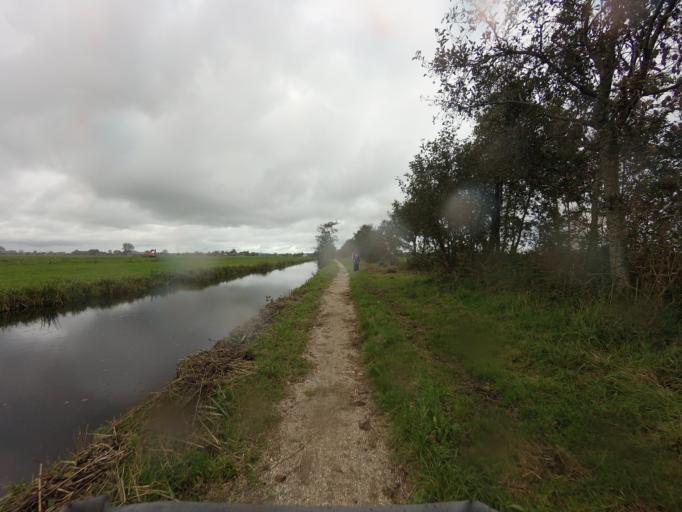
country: NL
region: South Holland
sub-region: Gemeente Alphen aan den Rijn
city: Alphen aan den Rijn
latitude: 52.1032
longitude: 4.6514
